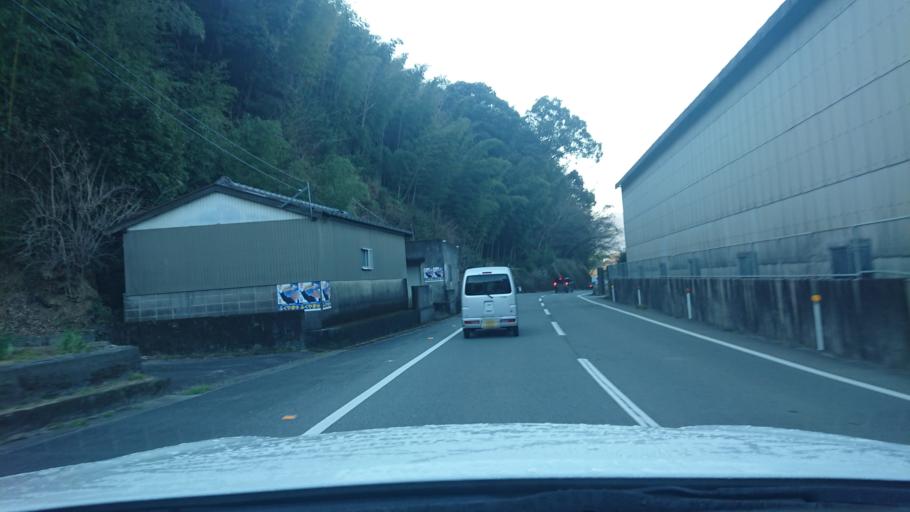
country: JP
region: Tokushima
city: Komatsushimacho
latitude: 33.9464
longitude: 134.5762
